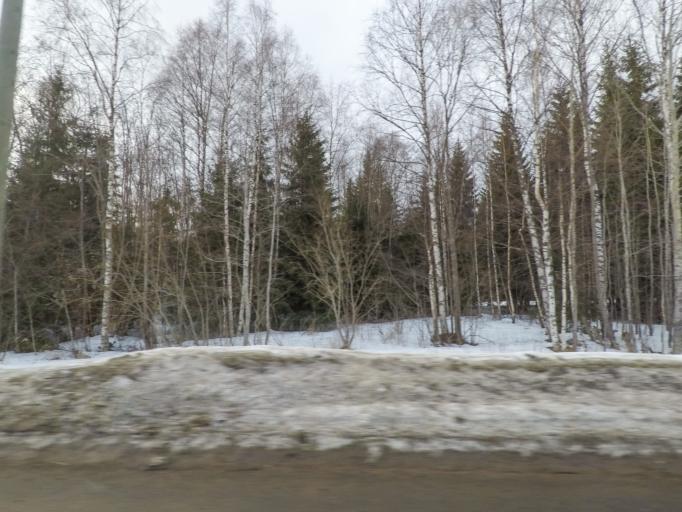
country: FI
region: Southern Savonia
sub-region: Mikkeli
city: Maentyharju
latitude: 61.4439
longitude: 26.6805
